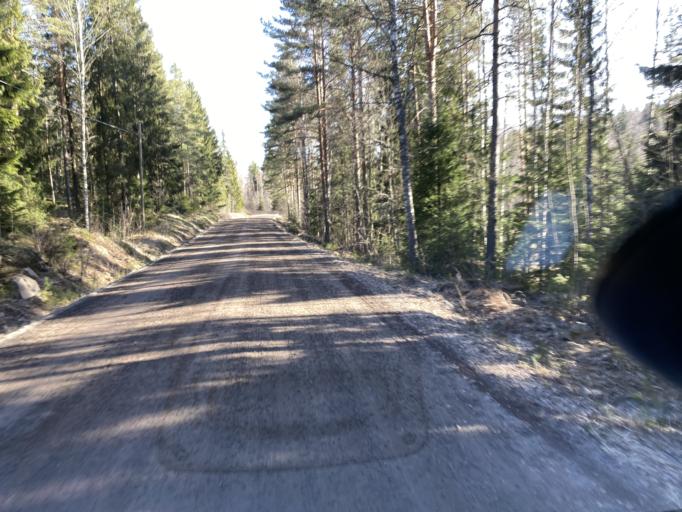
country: FI
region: Satakunta
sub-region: Rauma
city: Lappi
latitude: 61.1468
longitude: 21.9232
